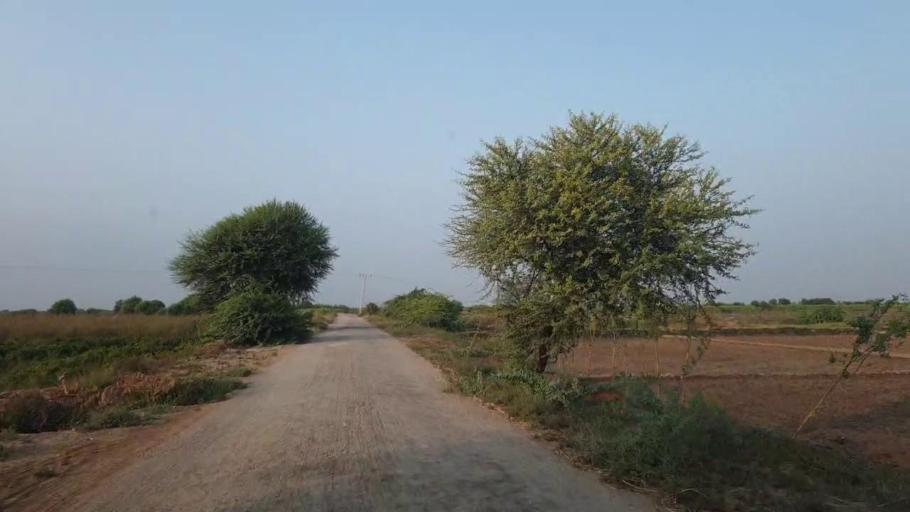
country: PK
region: Sindh
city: Tando Ghulam Ali
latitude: 25.0758
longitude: 68.9595
